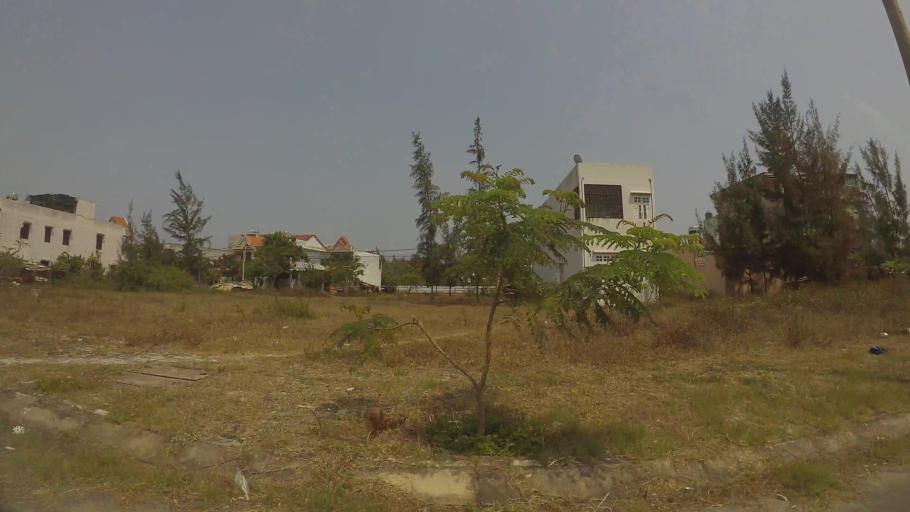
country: VN
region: Da Nang
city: Ngu Hanh Son
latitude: 15.9950
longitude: 108.2668
